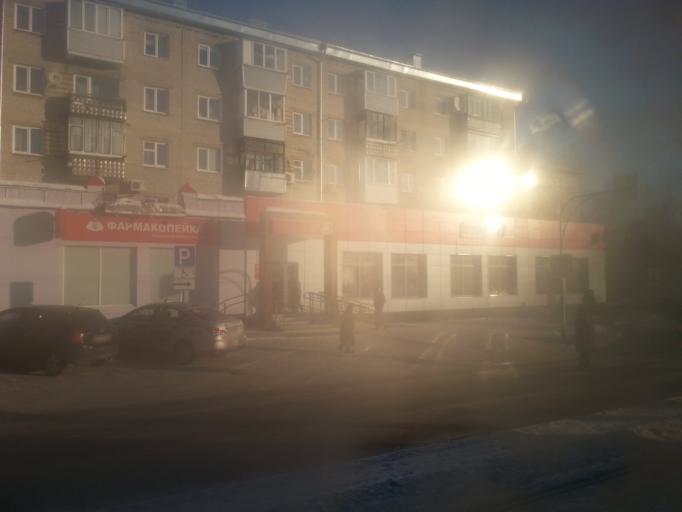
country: RU
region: Altai Krai
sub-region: Gorod Barnaulskiy
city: Barnaul
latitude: 53.3556
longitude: 83.7151
